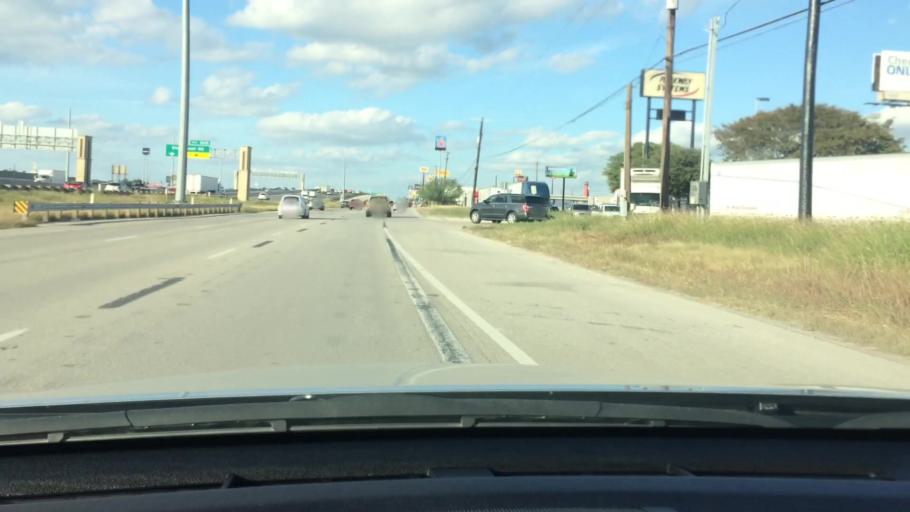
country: US
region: Texas
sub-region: Bexar County
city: Kirby
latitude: 29.4789
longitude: -98.4037
